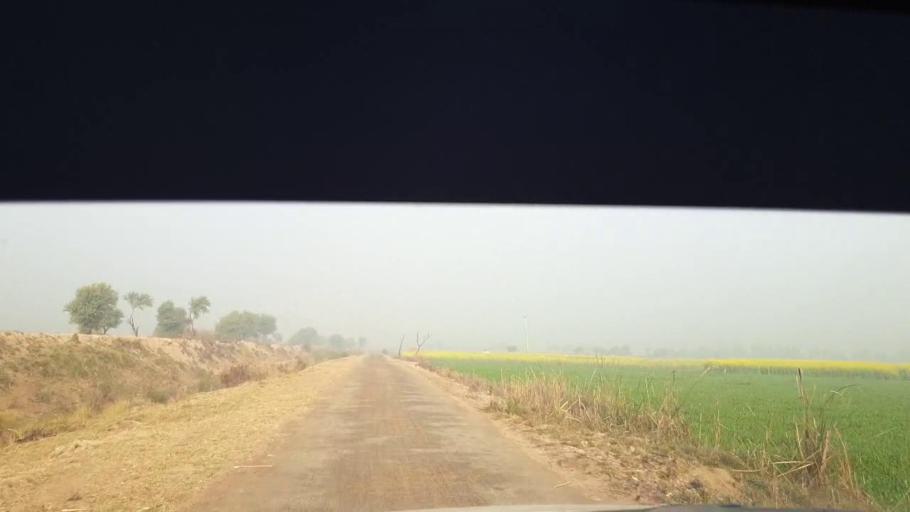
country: PK
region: Sindh
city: Berani
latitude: 25.7828
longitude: 68.7729
